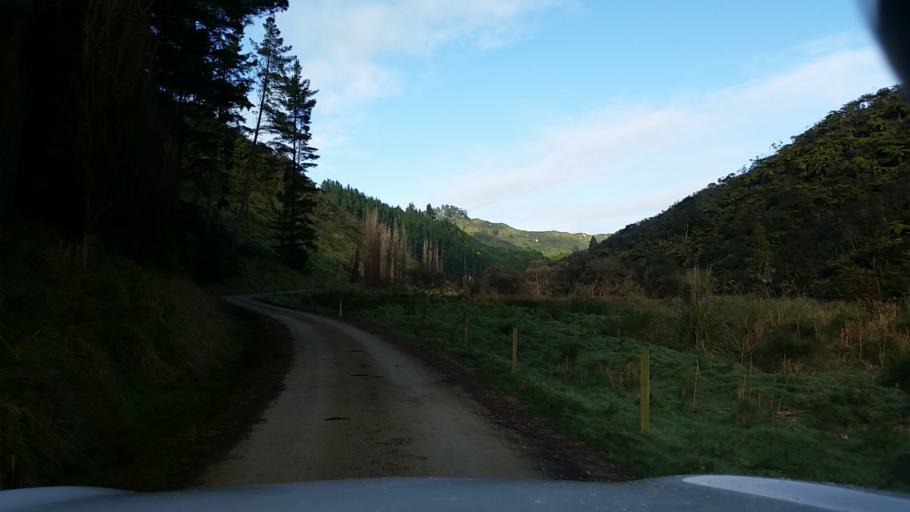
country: NZ
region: Taranaki
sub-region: South Taranaki District
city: Patea
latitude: -39.6840
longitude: 174.7640
